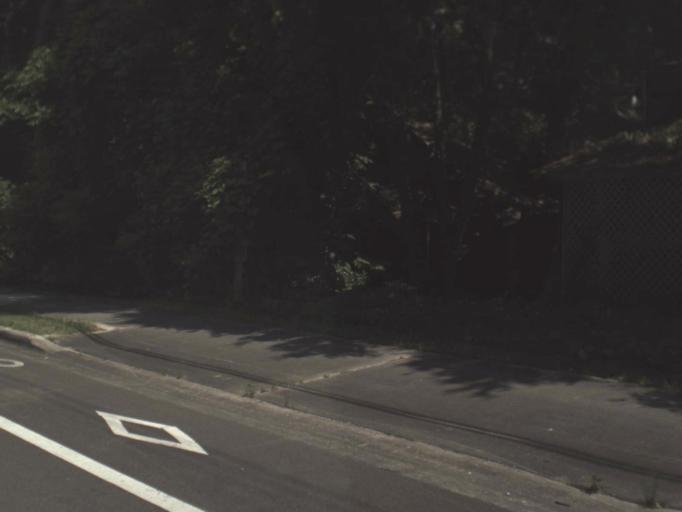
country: US
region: Florida
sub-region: Alachua County
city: Gainesville
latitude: 29.6396
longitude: -82.2823
